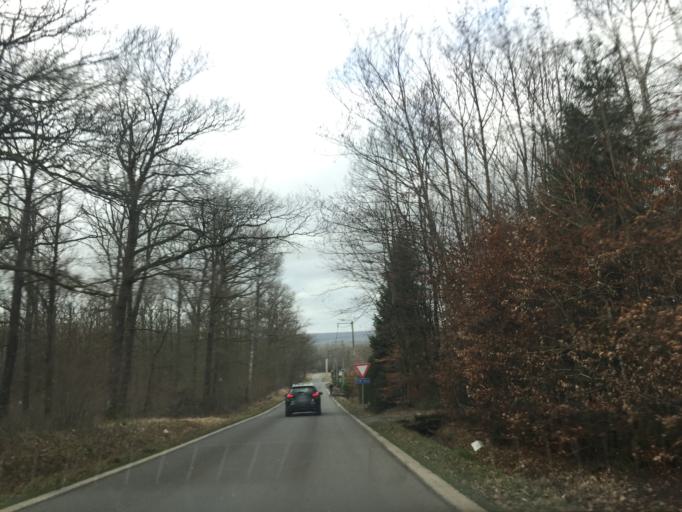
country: BE
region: Wallonia
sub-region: Province du Luxembourg
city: Durbuy
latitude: 50.3227
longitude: 5.4805
